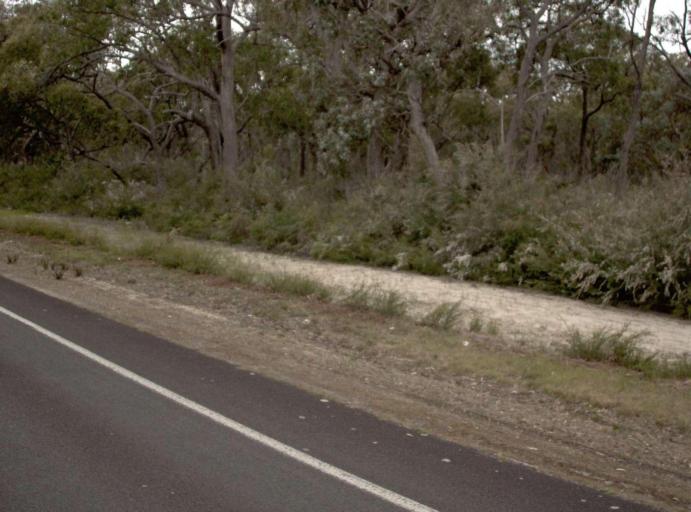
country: AU
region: Victoria
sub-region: Wellington
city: Sale
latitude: -38.3358
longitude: 147.0130
